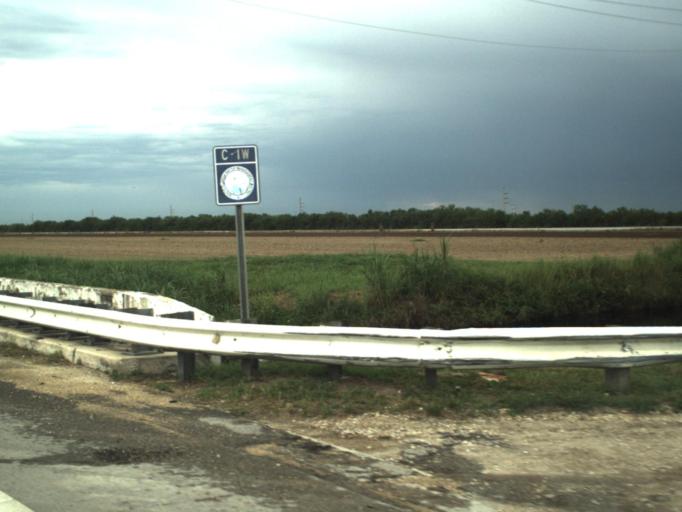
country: US
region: Florida
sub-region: Miami-Dade County
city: The Hammocks
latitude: 25.6608
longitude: -80.4808
